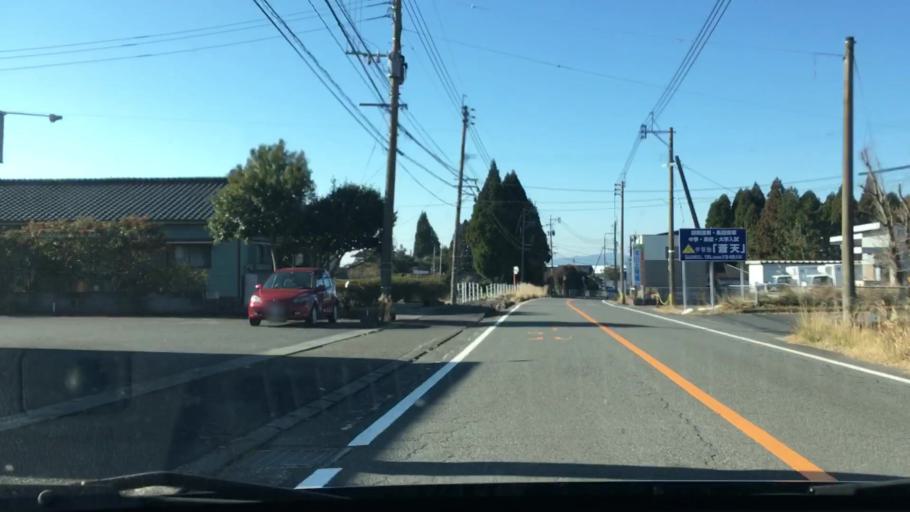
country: JP
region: Kagoshima
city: Kajiki
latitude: 31.7886
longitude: 130.7105
